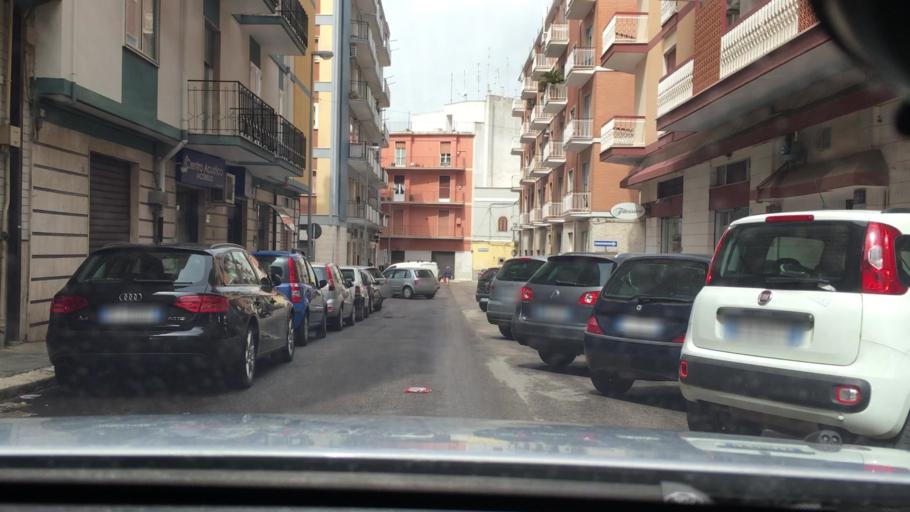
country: IT
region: Apulia
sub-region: Provincia di Bari
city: Gioia del Colle
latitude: 40.7965
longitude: 16.9210
